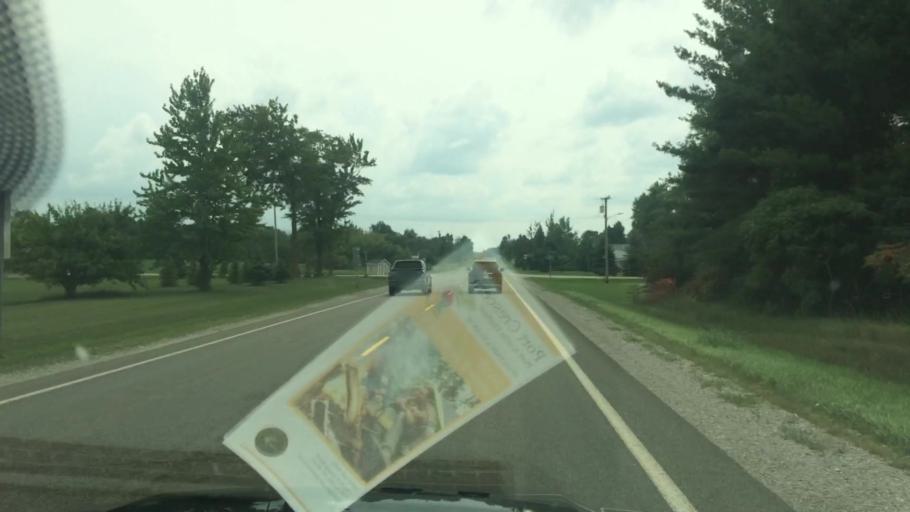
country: US
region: Michigan
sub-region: Tuscola County
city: Cass City
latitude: 43.6772
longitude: -83.0982
